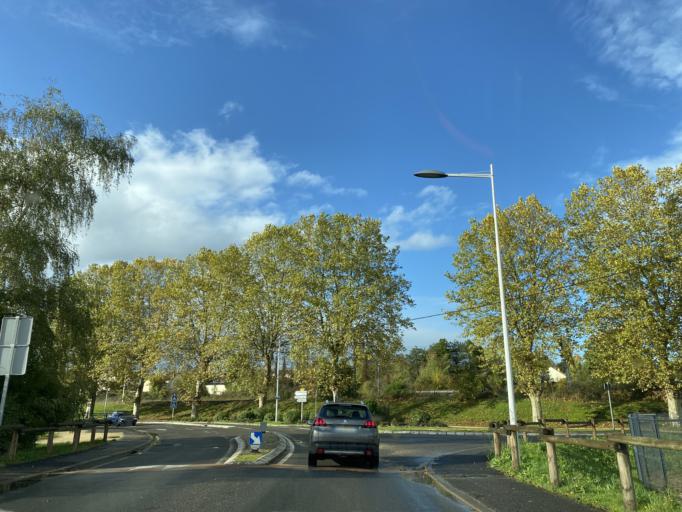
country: FR
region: Centre
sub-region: Departement du Cher
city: Bourges
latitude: 47.0946
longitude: 2.3788
